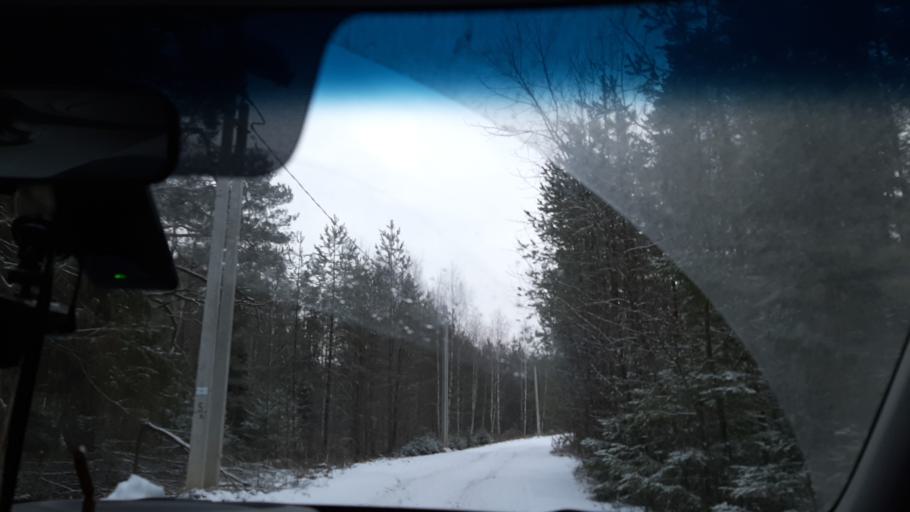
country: RU
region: Ivanovo
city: Kokhma
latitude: 56.8985
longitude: 41.0108
